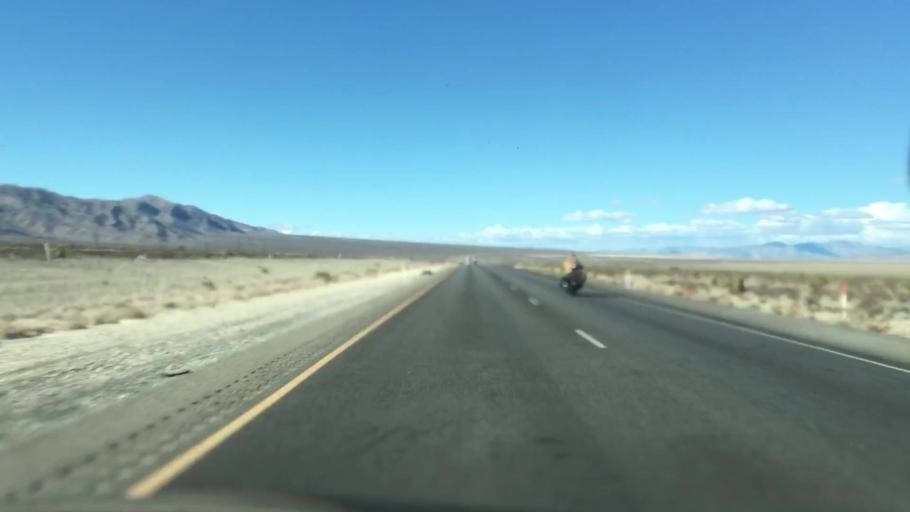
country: US
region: Nevada
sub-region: Clark County
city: Summerlin South
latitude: 36.3826
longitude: -115.3758
